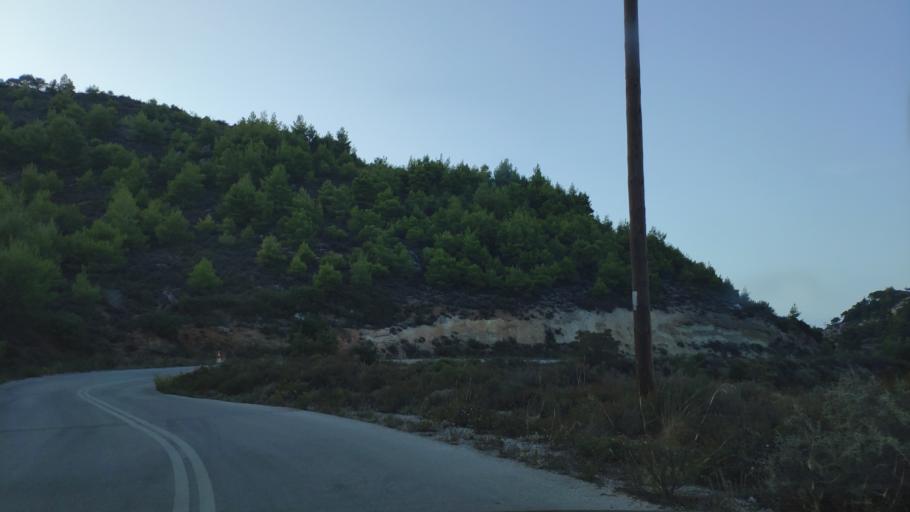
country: GR
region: West Greece
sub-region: Nomos Achaias
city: Aiyira
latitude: 38.0949
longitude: 22.4089
